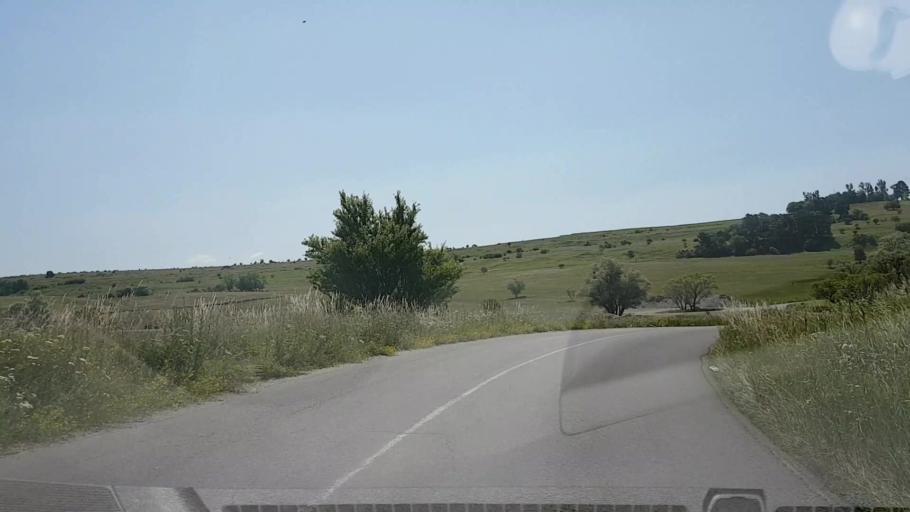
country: RO
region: Brasov
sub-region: Comuna Cincu
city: Cincu
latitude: 45.9540
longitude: 24.7824
